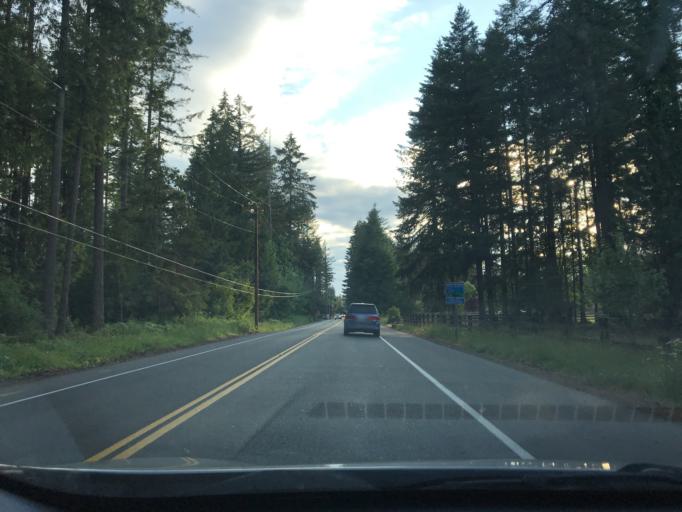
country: US
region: Washington
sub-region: King County
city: Lake Morton-Berrydale
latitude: 47.2976
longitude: -122.0610
